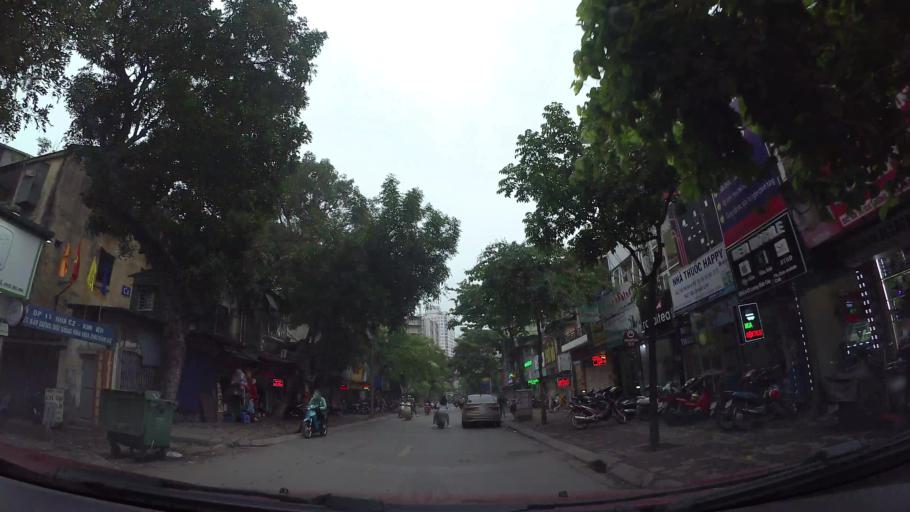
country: VN
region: Ha Noi
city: Hai BaTrung
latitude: 21.0047
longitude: 105.8357
